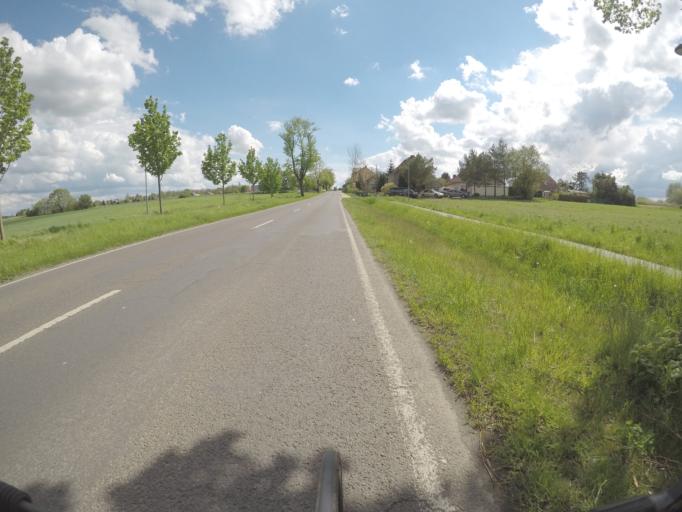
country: DE
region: Brandenburg
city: Bernau bei Berlin
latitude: 52.6925
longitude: 13.5885
